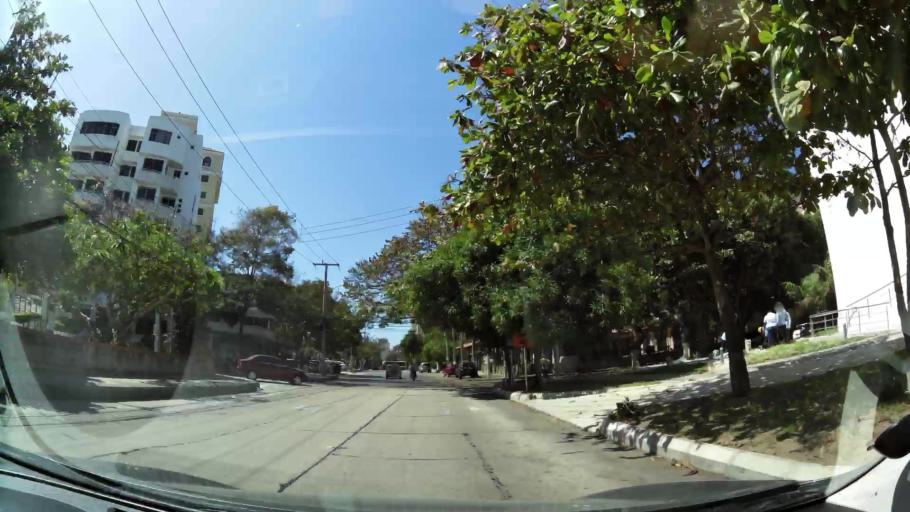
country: CO
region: Atlantico
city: Barranquilla
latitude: 10.9990
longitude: -74.7989
